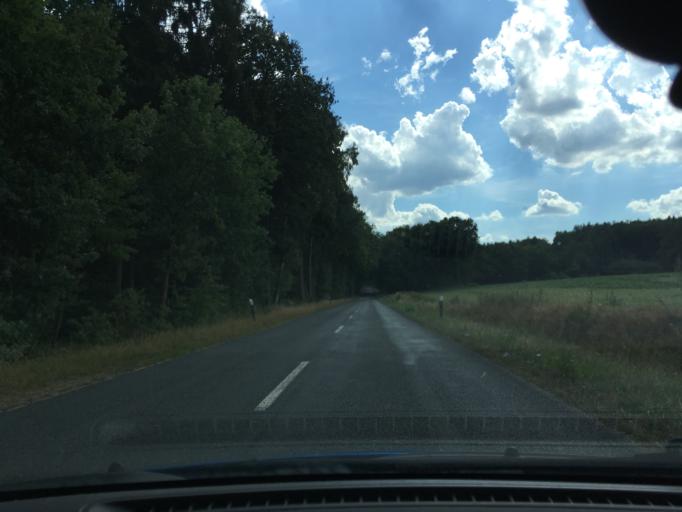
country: DE
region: Lower Saxony
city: Rehlingen
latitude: 53.1013
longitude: 10.2144
